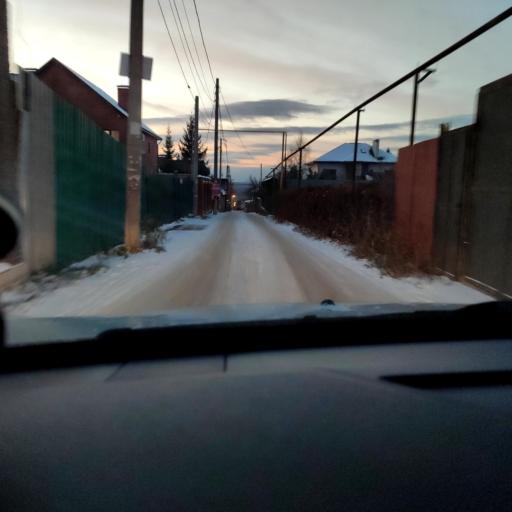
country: RU
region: Samara
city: Samara
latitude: 53.2580
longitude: 50.2015
